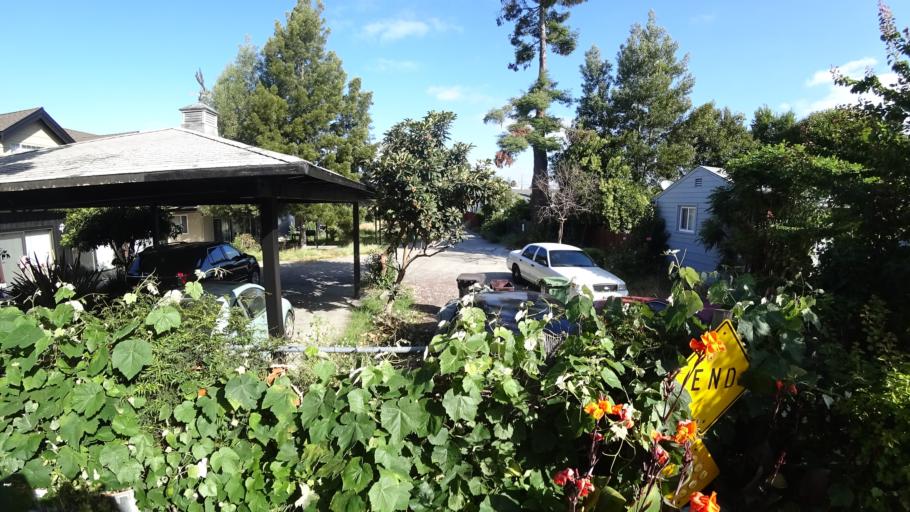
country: US
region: California
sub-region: Alameda County
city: Cherryland
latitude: 37.6815
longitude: -122.0918
